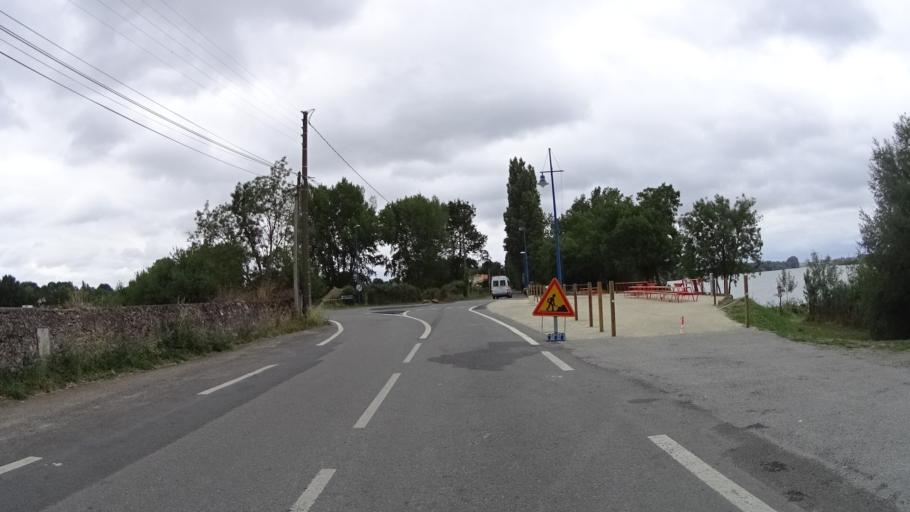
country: FR
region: Pays de la Loire
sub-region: Departement de la Loire-Atlantique
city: Sainte-Luce-sur-Loire
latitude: 47.2404
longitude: -1.4676
